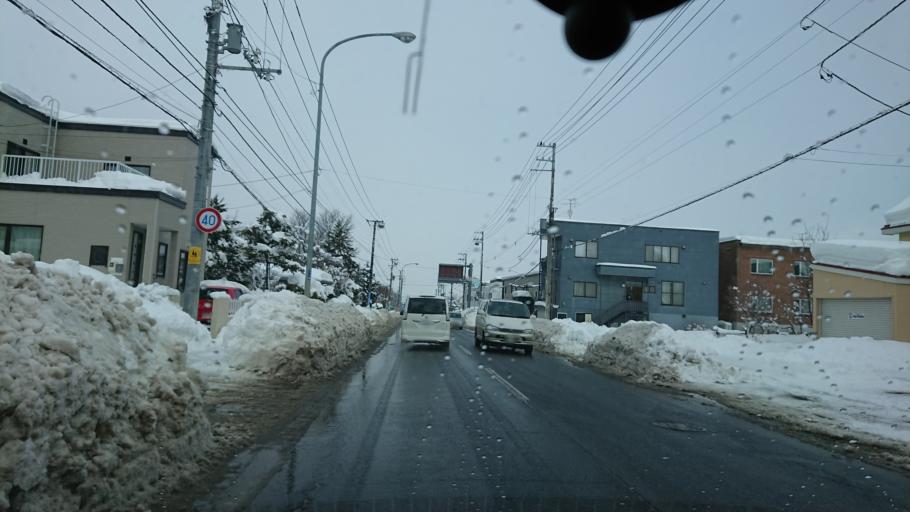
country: JP
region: Hokkaido
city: Sapporo
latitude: 42.9693
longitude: 141.3431
